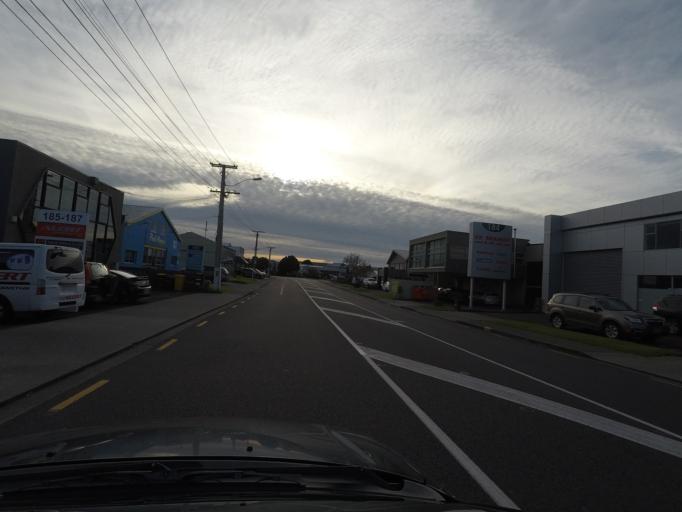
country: NZ
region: Auckland
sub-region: Auckland
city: Tamaki
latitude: -36.8928
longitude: 174.8322
